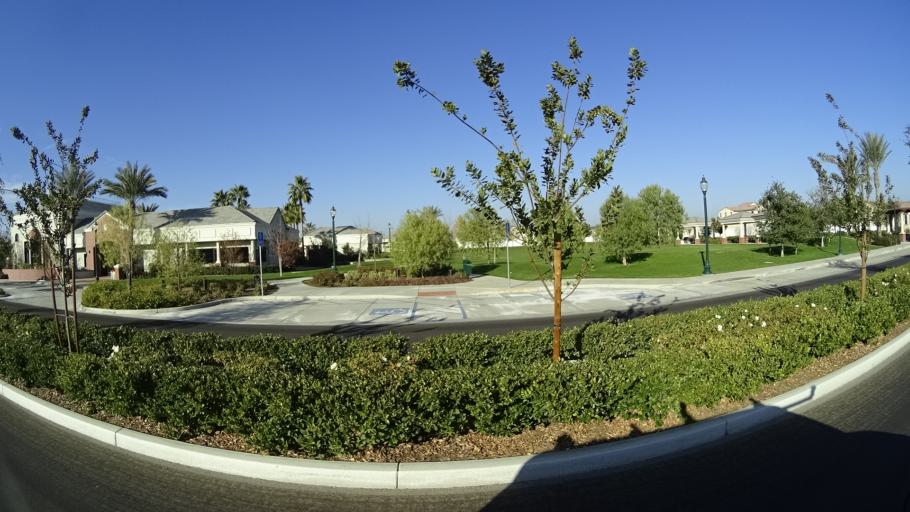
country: US
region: California
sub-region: Kern County
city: Rosedale
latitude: 35.3373
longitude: -119.1562
